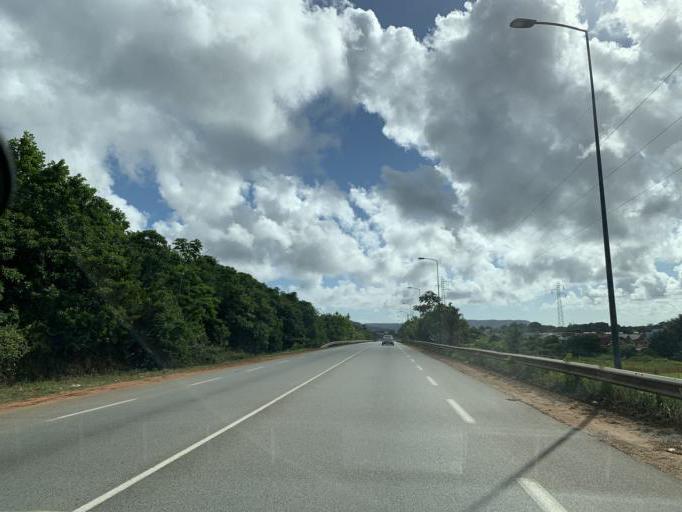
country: GF
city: Macouria
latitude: 4.8916
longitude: -52.3427
